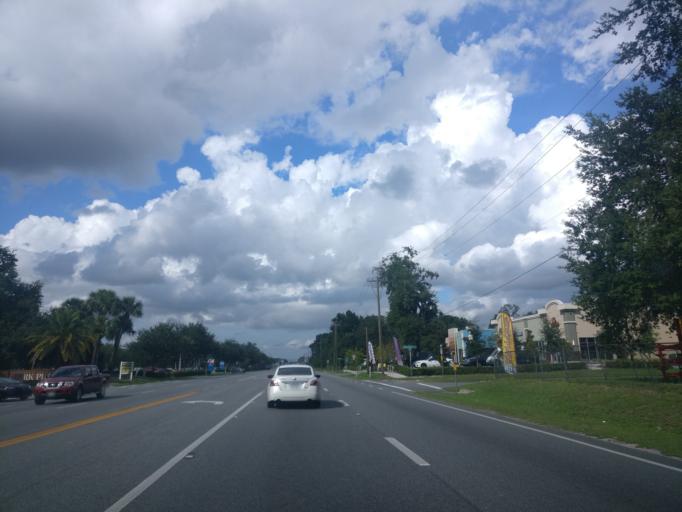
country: US
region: Florida
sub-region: Osceola County
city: Kissimmee
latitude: 28.3139
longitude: -81.4037
